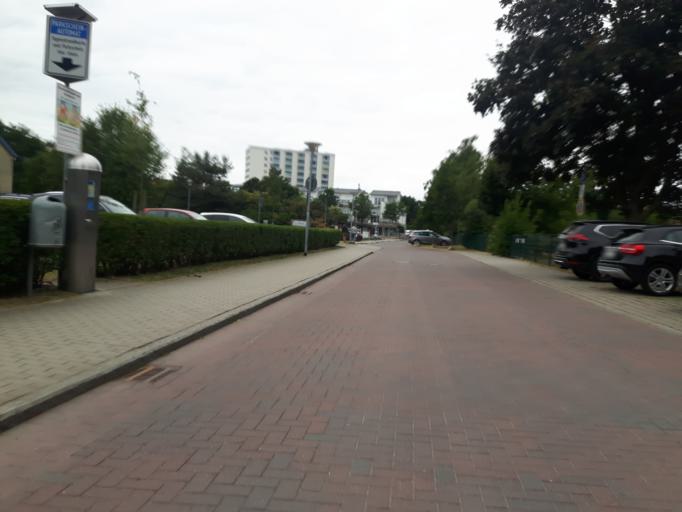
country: DE
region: Schleswig-Holstein
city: Schashagen
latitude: 54.0887
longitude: 10.8612
